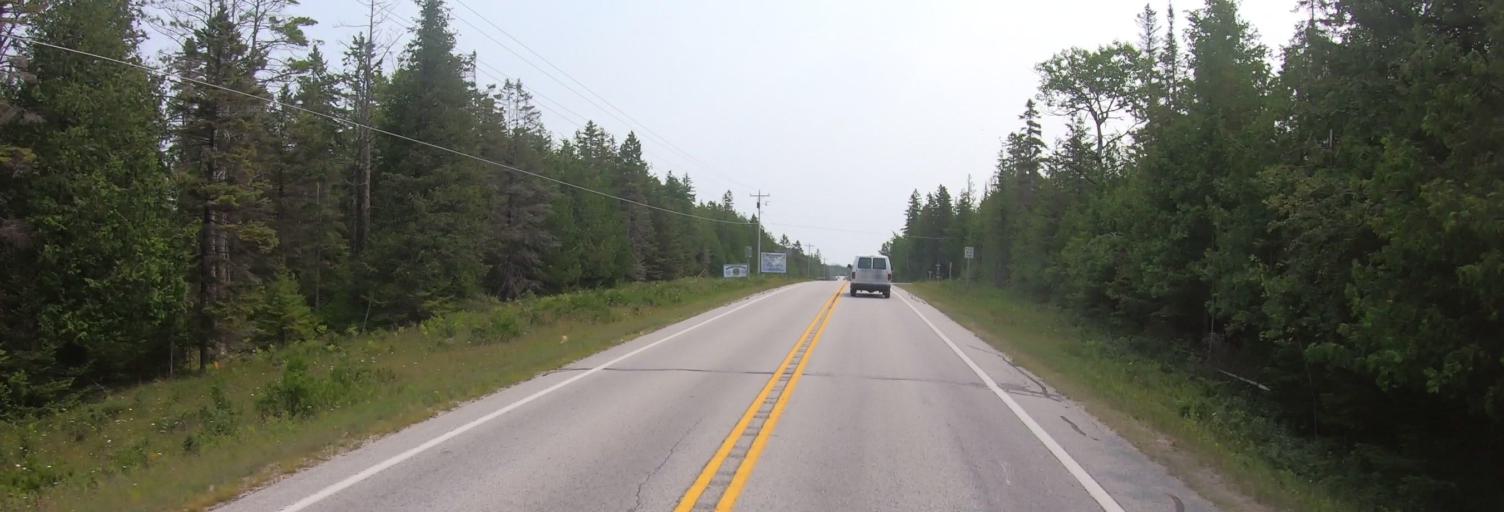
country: CA
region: Ontario
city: Thessalon
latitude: 45.9972
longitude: -83.8493
